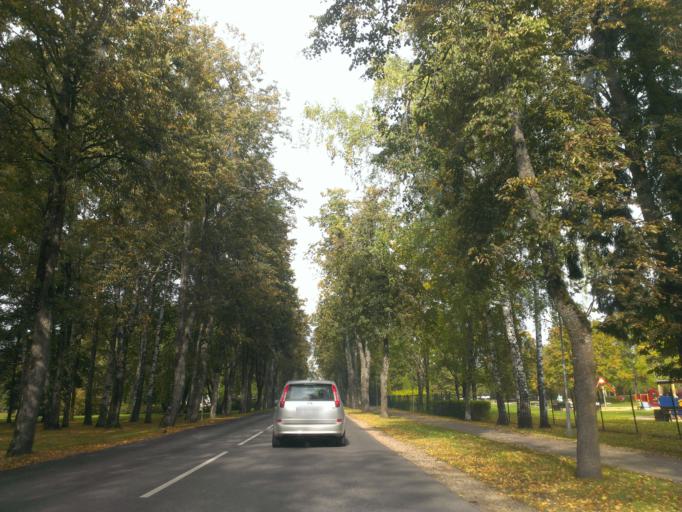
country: LV
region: Sigulda
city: Sigulda
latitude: 57.1572
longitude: 24.8541
